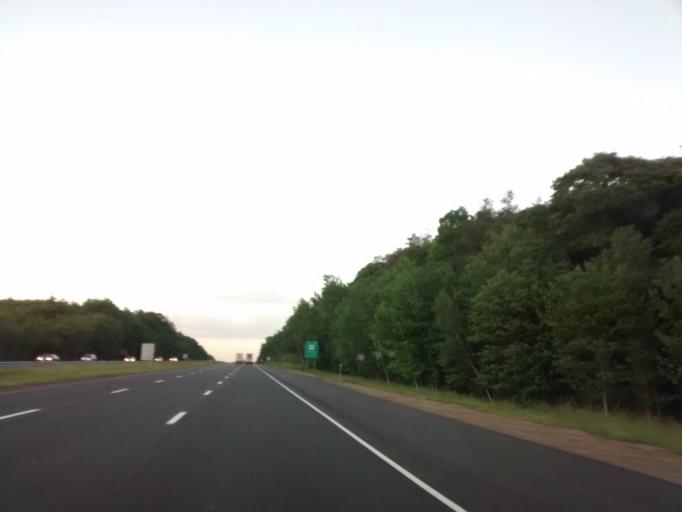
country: US
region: Connecticut
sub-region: Tolland County
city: Stafford
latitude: 41.9644
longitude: -72.1912
